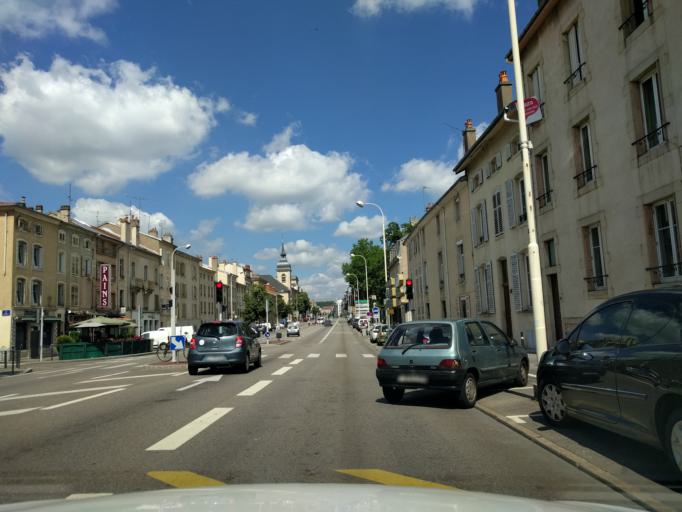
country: FR
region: Lorraine
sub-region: Departement de Meurthe-et-Moselle
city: Nancy
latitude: 48.6811
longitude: 6.1939
